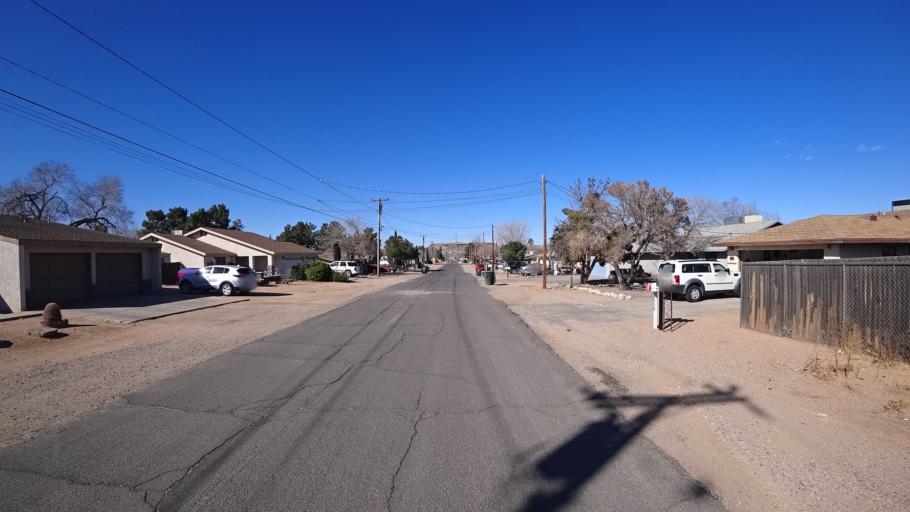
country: US
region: Arizona
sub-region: Mohave County
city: Kingman
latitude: 35.1972
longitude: -114.0183
